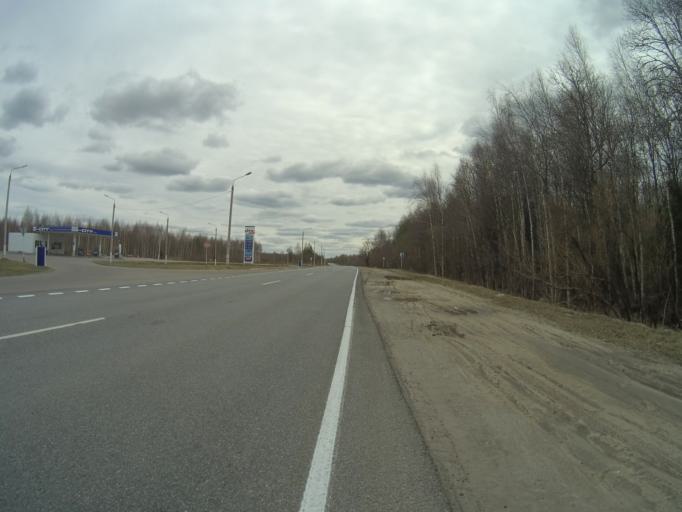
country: RU
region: Vladimir
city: Golovino
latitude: 55.9655
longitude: 40.5530
